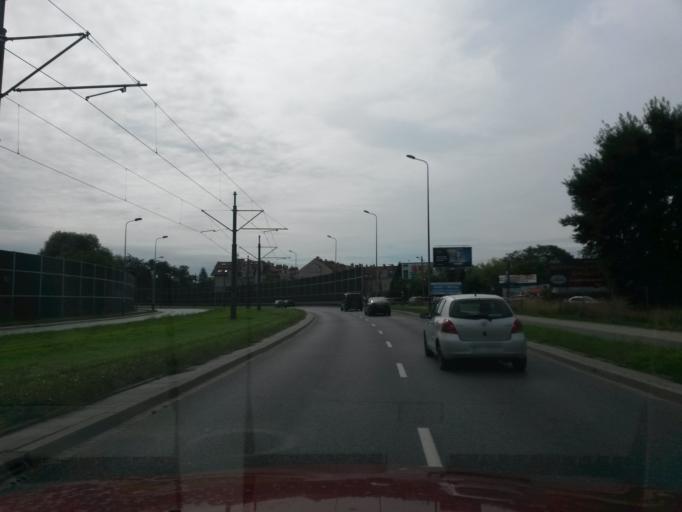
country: PL
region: Lesser Poland Voivodeship
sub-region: Krakow
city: Krakow
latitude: 50.0426
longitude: 19.9743
